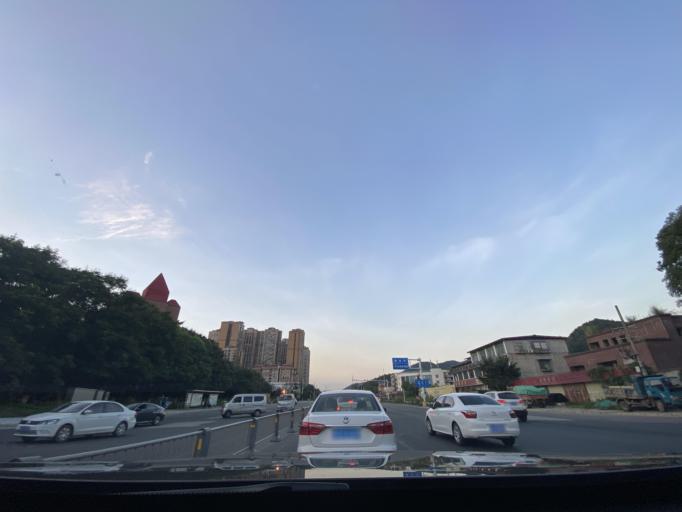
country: CN
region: Sichuan
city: Longquan
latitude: 30.6014
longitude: 104.3097
